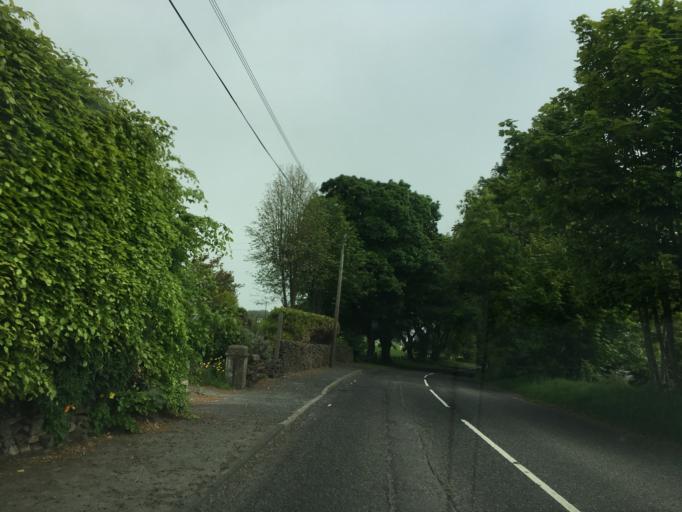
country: GB
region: Scotland
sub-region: The Scottish Borders
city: West Linton
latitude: 55.7076
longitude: -3.3539
